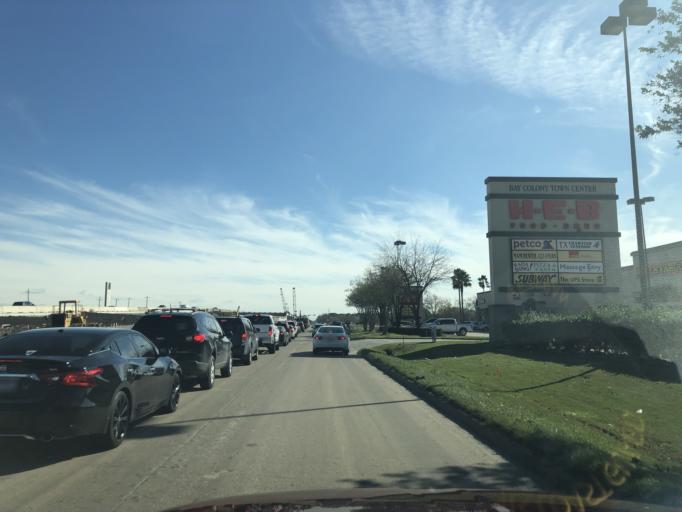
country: US
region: Texas
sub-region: Galveston County
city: League City
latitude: 29.4685
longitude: -95.0933
